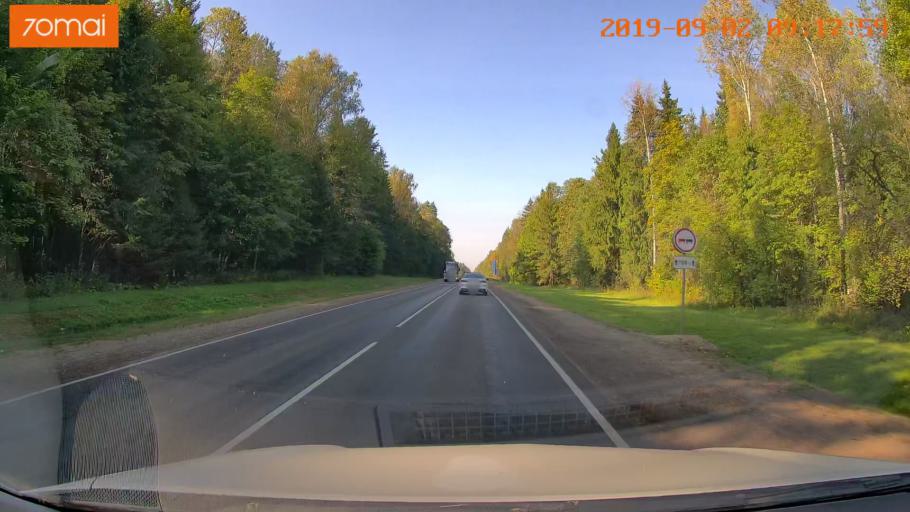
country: RU
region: Kaluga
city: Nikola-Lenivets
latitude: 54.8198
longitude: 35.4388
